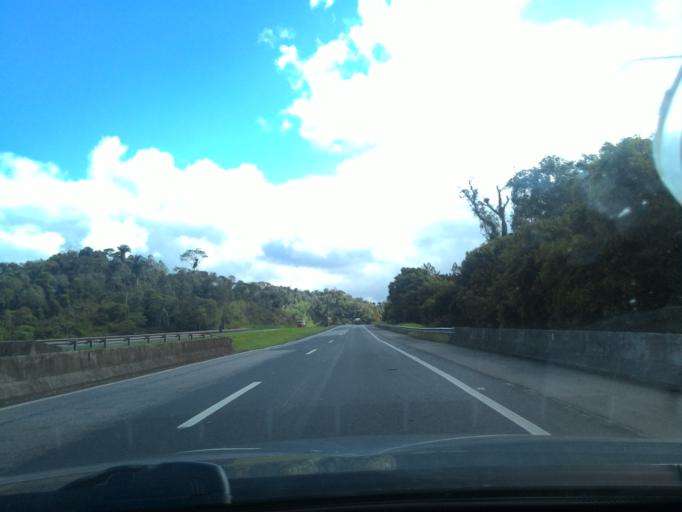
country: BR
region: Sao Paulo
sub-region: Cajati
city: Cajati
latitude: -24.9467
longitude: -48.3131
